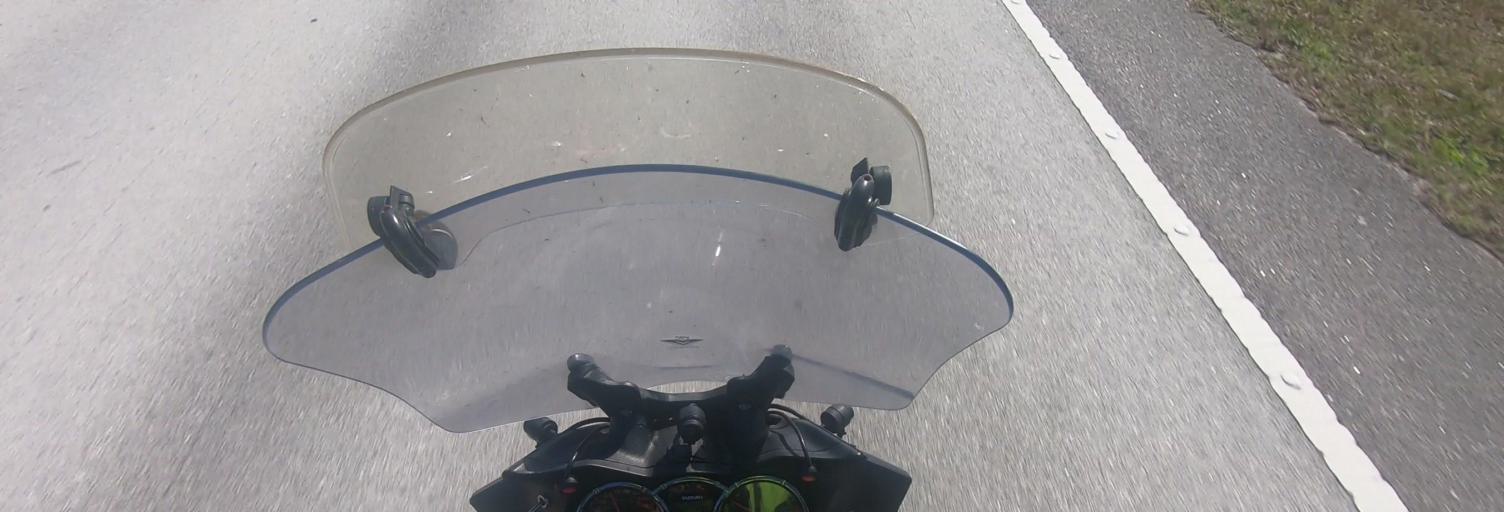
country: US
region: Florida
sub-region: Collier County
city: Marco
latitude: 25.8694
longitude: -81.1712
